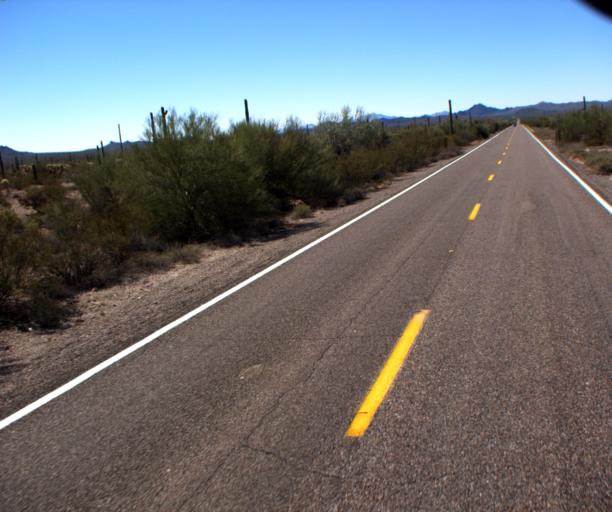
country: MX
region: Sonora
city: Sonoyta
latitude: 32.0649
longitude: -112.7855
